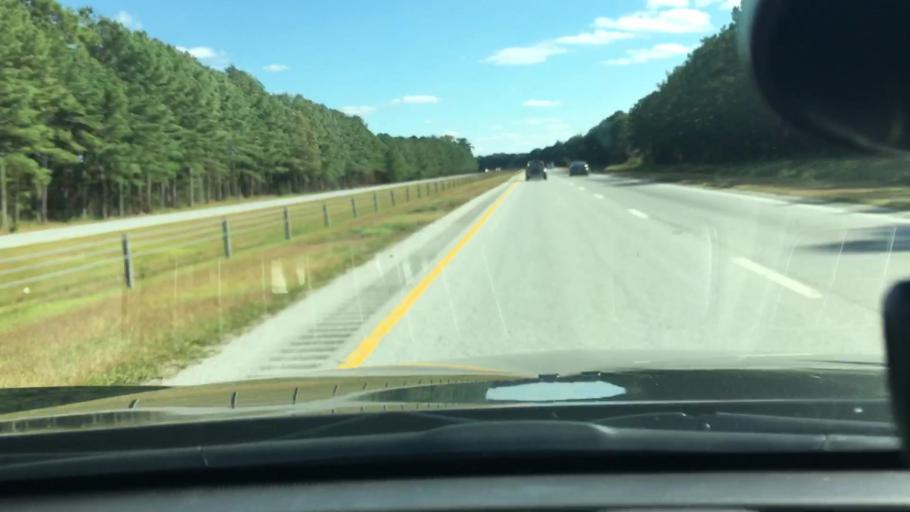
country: US
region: North Carolina
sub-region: Pitt County
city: Farmville
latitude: 35.6313
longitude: -77.7188
